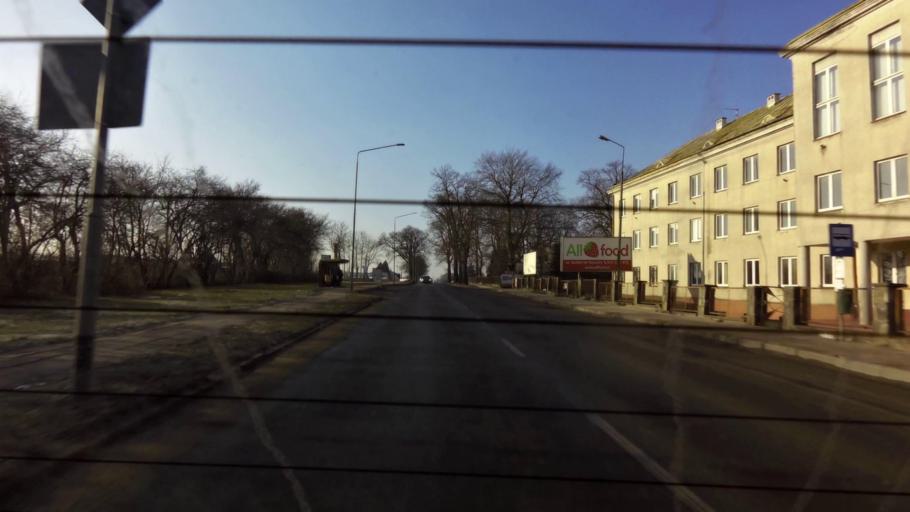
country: PL
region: West Pomeranian Voivodeship
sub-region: Koszalin
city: Koszalin
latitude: 54.1848
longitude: 16.1582
